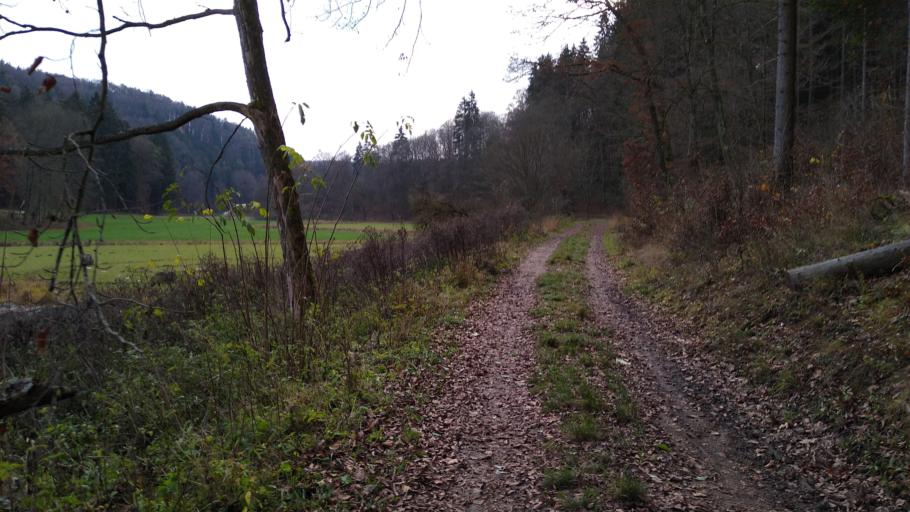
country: DE
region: Bavaria
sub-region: Upper Palatinate
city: Seubersdorf
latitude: 49.1028
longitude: 11.5993
